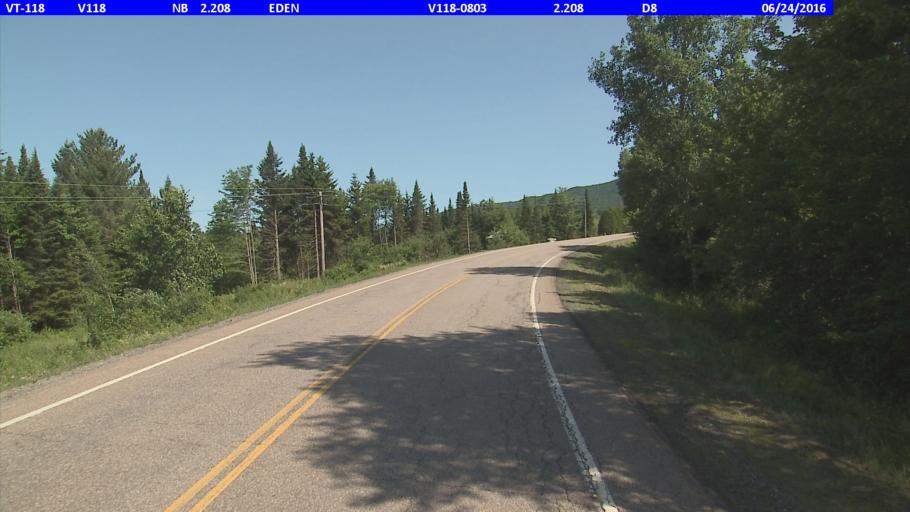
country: US
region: Vermont
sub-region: Lamoille County
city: Hyde Park
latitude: 44.7346
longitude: -72.5674
